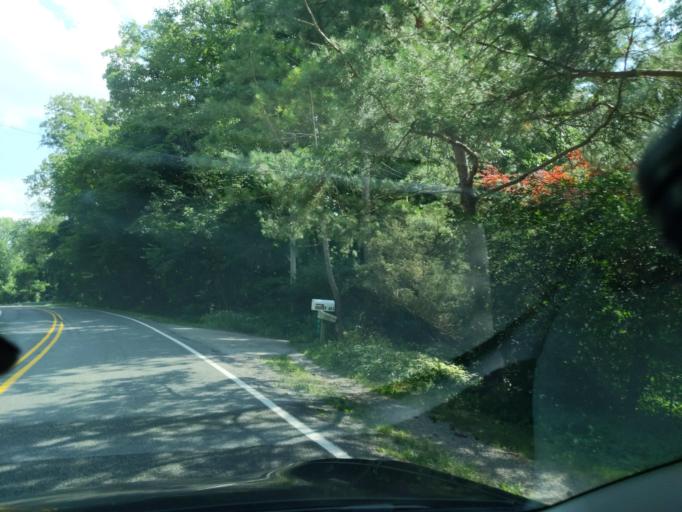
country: US
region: Michigan
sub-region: Kent County
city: Forest Hills
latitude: 42.9708
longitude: -85.5328
